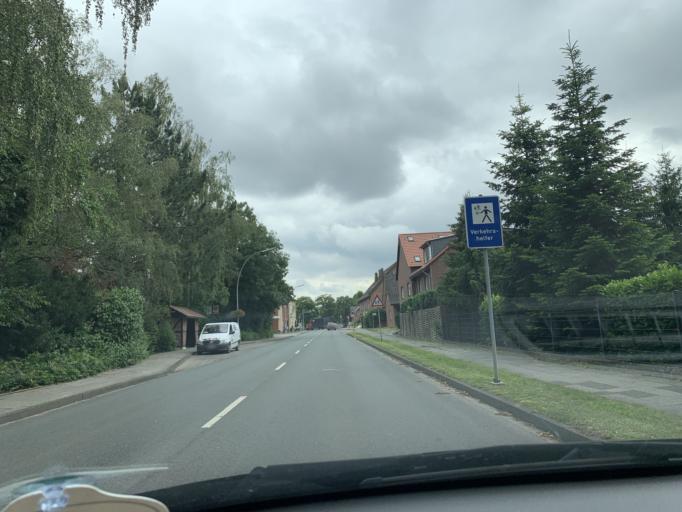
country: DE
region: North Rhine-Westphalia
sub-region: Regierungsbezirk Munster
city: Wadersloh
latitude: 51.7134
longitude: 8.2624
